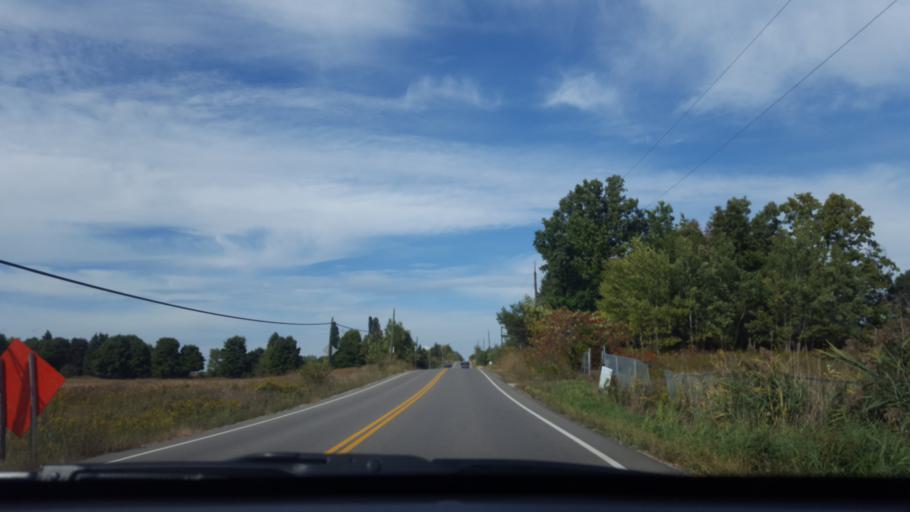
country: CA
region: Ontario
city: Vaughan
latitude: 43.8491
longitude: -79.5885
